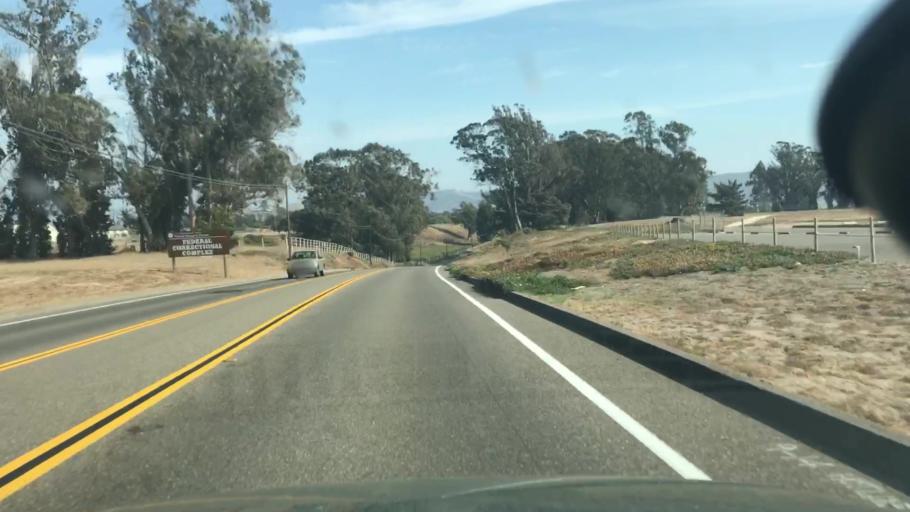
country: US
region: California
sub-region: Santa Barbara County
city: Vandenberg Village
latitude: 34.6775
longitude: -120.4965
